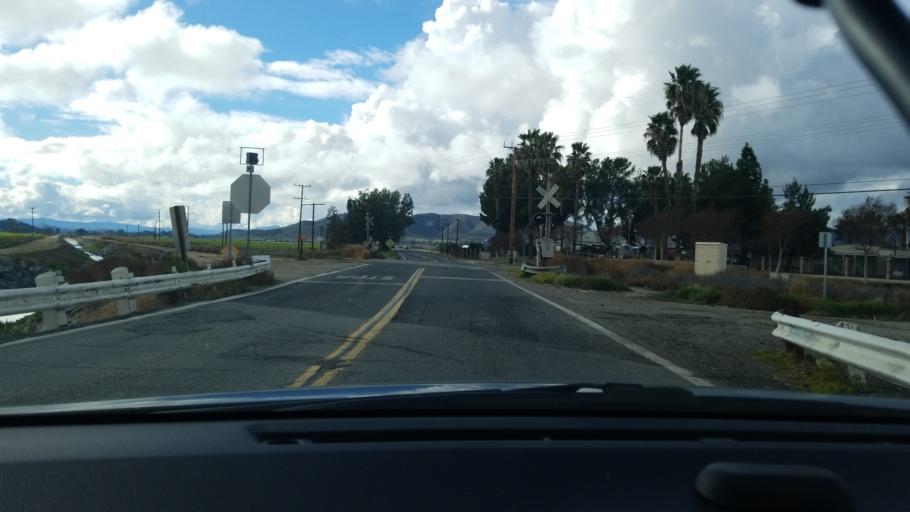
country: US
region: California
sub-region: Riverside County
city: Hemet
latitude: 33.7293
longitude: -117.0204
